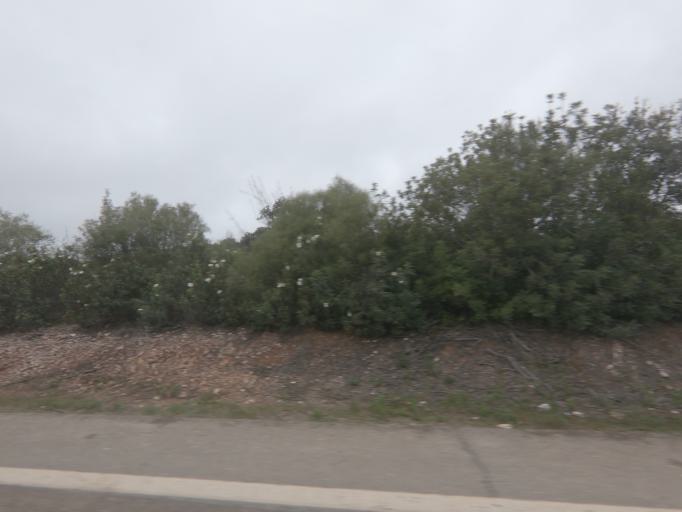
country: ES
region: Extremadura
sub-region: Provincia de Badajoz
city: Puebla de Obando
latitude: 39.2815
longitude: -6.5216
